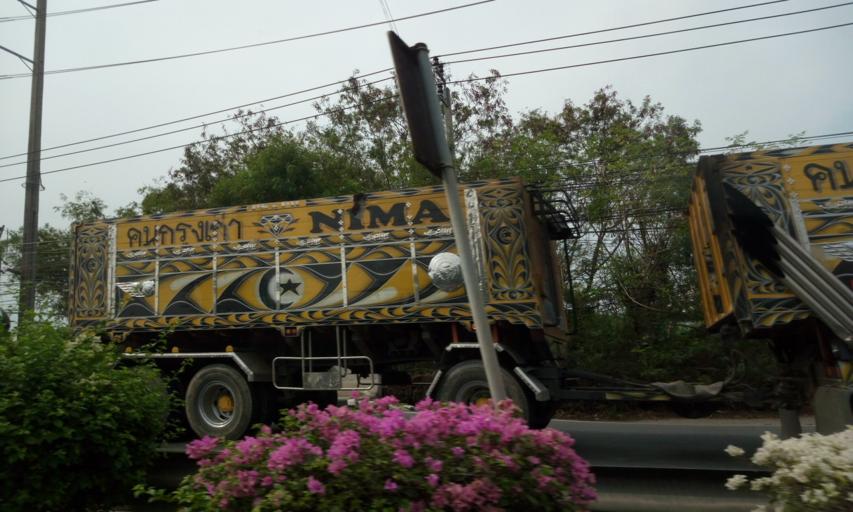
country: TH
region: Bangkok
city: Lat Krabang
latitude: 13.7226
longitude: 100.7522
